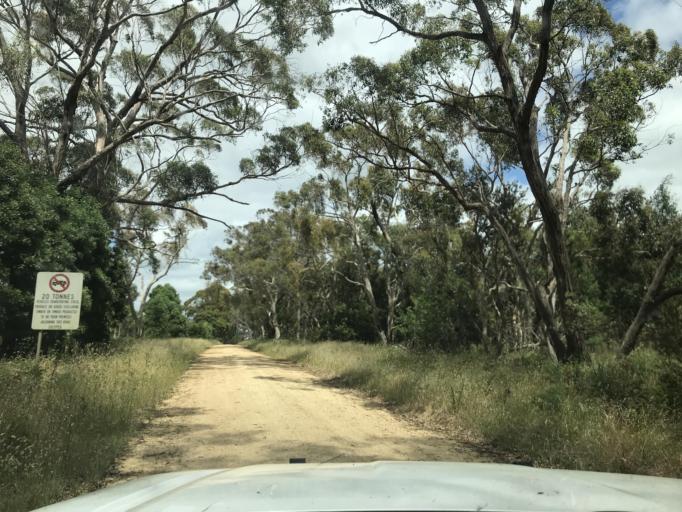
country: AU
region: South Australia
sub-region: Wattle Range
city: Penola
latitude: -37.2975
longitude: 141.0086
